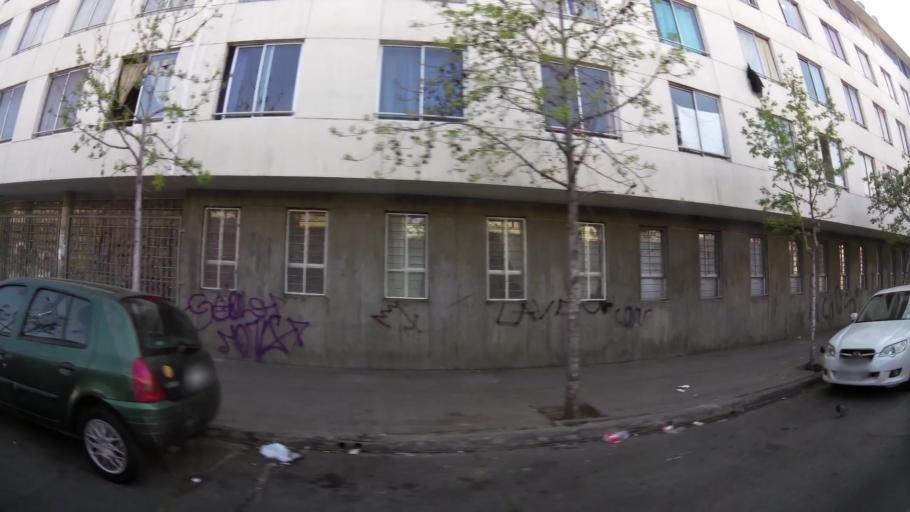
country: CL
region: Santiago Metropolitan
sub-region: Provincia de Santiago
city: Santiago
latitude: -33.4368
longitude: -70.6737
